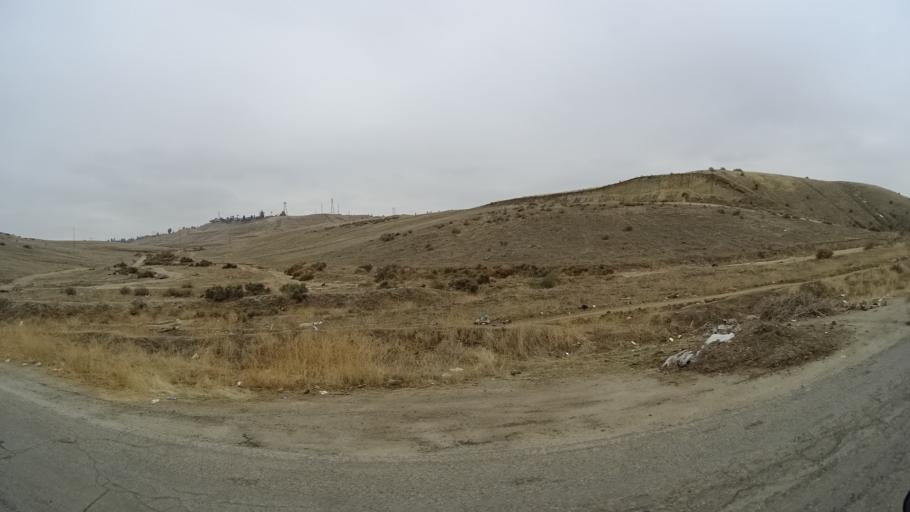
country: US
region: California
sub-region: Kern County
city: Oildale
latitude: 35.4234
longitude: -118.9391
